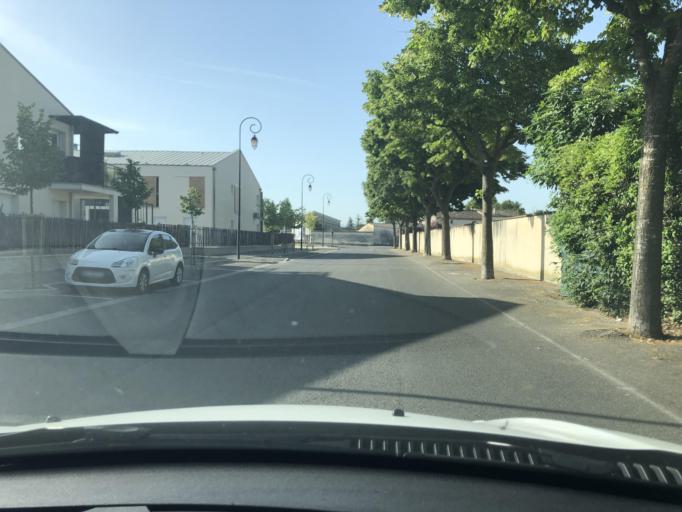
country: FR
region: Provence-Alpes-Cote d'Azur
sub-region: Departement du Vaucluse
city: Velleron
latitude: 43.9588
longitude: 5.0324
